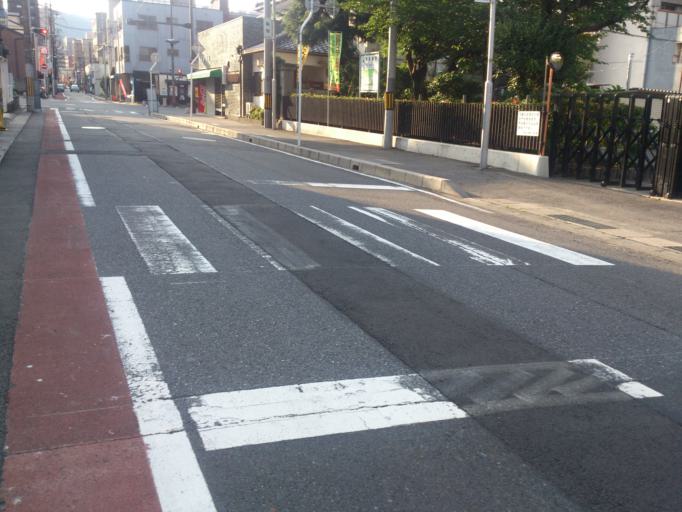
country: JP
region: Shiga Prefecture
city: Otsu-shi
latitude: 35.0077
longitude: 135.8686
